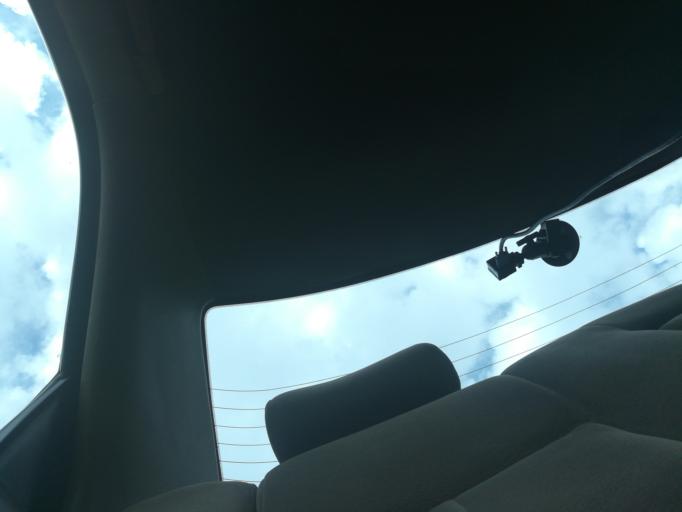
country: NG
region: Lagos
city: Ikorodu
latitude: 6.6602
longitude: 3.5879
